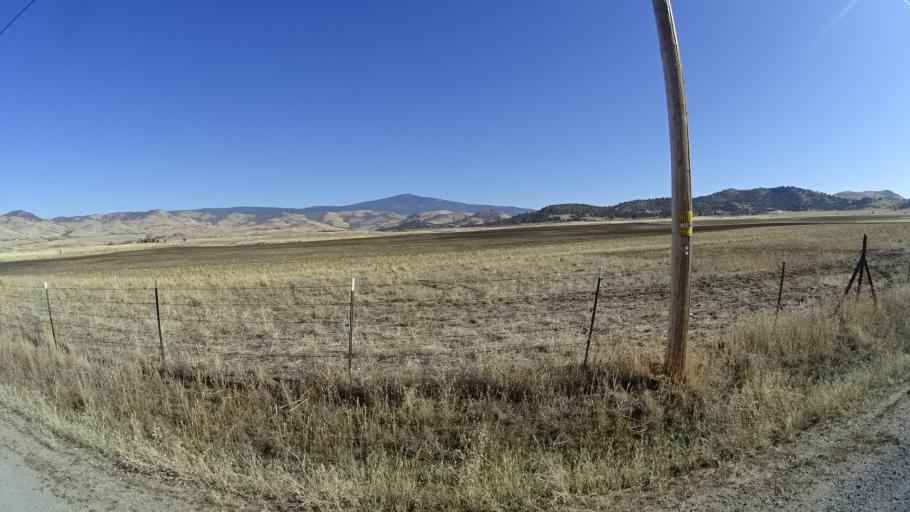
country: US
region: California
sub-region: Siskiyou County
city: Montague
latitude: 41.8029
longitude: -122.4158
